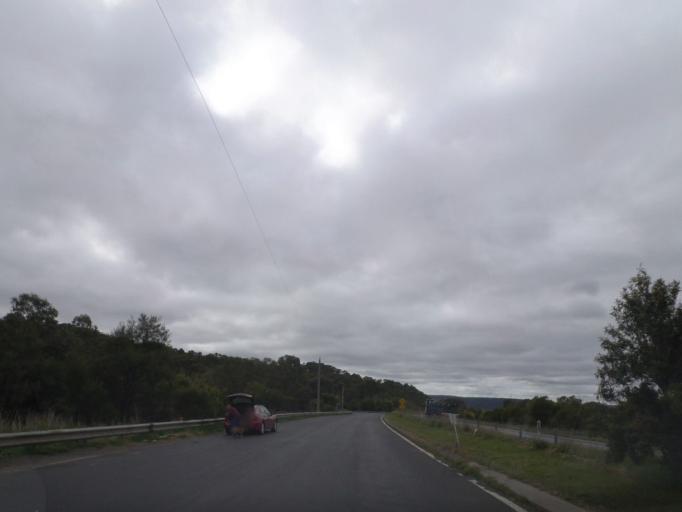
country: AU
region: Victoria
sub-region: Whittlesea
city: Whittlesea
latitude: -37.3220
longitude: 145.0351
